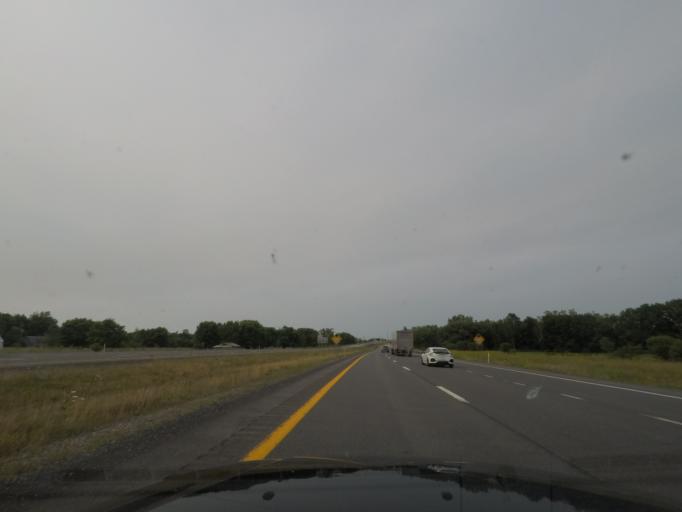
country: US
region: New York
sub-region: Clinton County
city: Champlain
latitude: 44.9848
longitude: -73.4577
